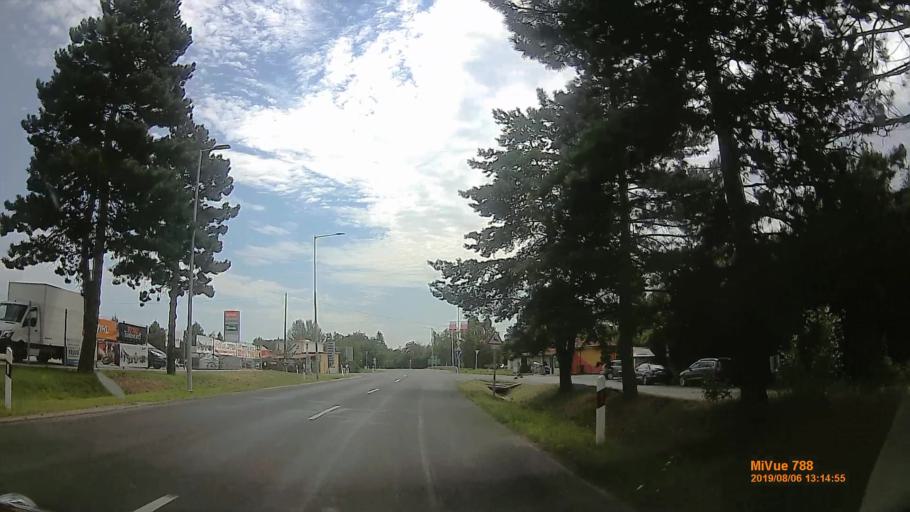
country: HU
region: Vas
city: Koszeg
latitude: 47.4025
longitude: 16.5377
